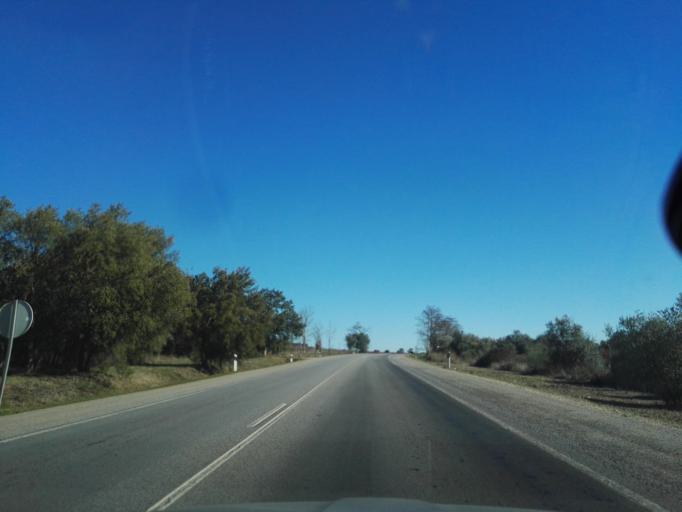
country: PT
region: Evora
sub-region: Estremoz
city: Estremoz
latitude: 38.8325
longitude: -7.5426
